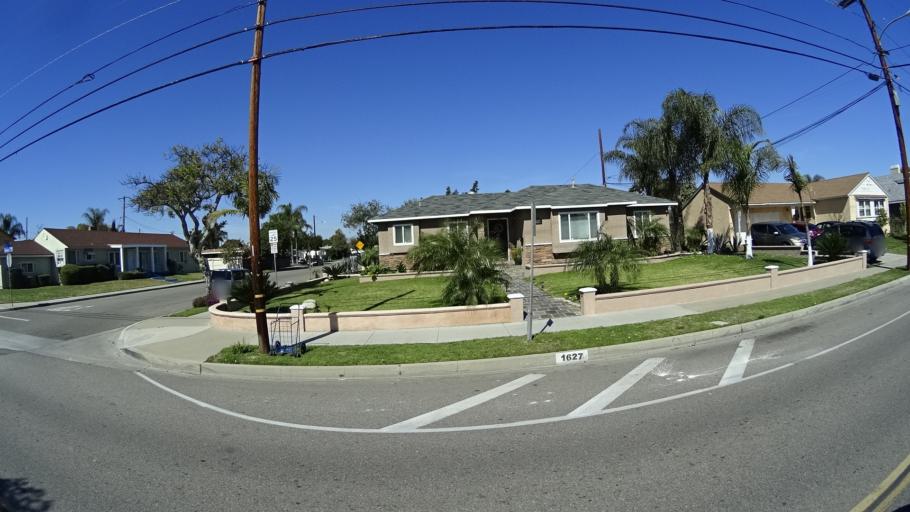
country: US
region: California
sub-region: Orange County
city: Anaheim
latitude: 33.8355
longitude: -117.8937
